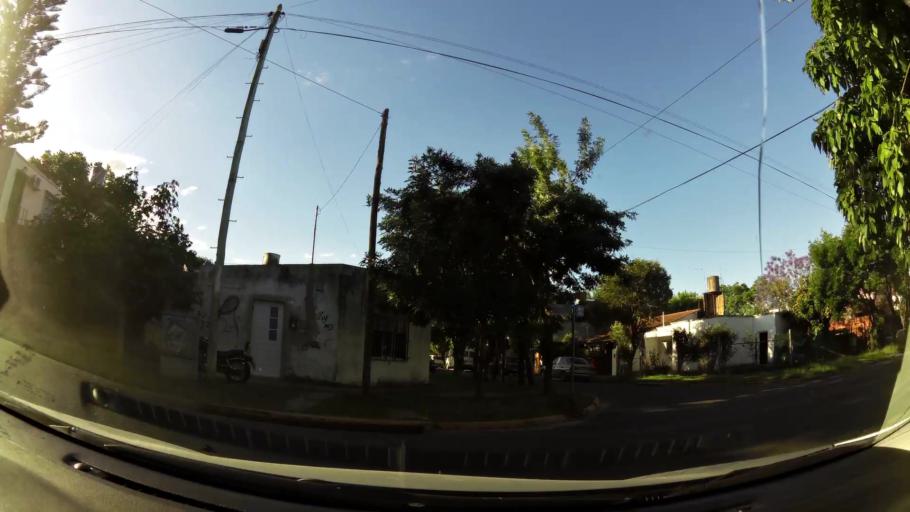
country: AR
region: Buenos Aires
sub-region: Partido de Tigre
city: Tigre
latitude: -34.4610
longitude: -58.5653
